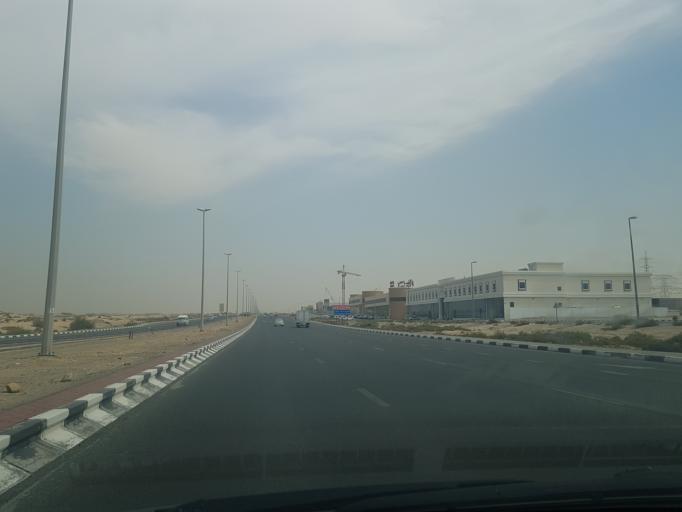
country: AE
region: Ash Shariqah
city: Sharjah
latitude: 25.2592
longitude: 55.5112
